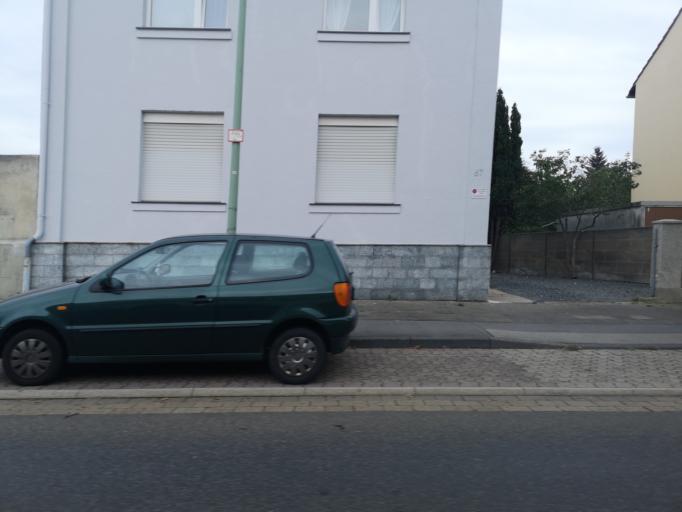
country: DE
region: North Rhine-Westphalia
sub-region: Regierungsbezirk Koln
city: Kreuzau
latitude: 50.7731
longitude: 6.4920
